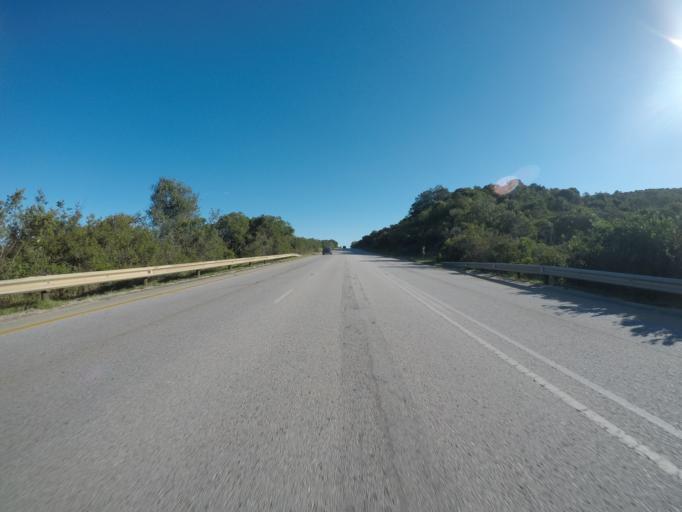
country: ZA
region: Eastern Cape
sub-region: Cacadu District Municipality
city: Jeffrey's Bay
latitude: -33.9057
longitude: 25.0773
